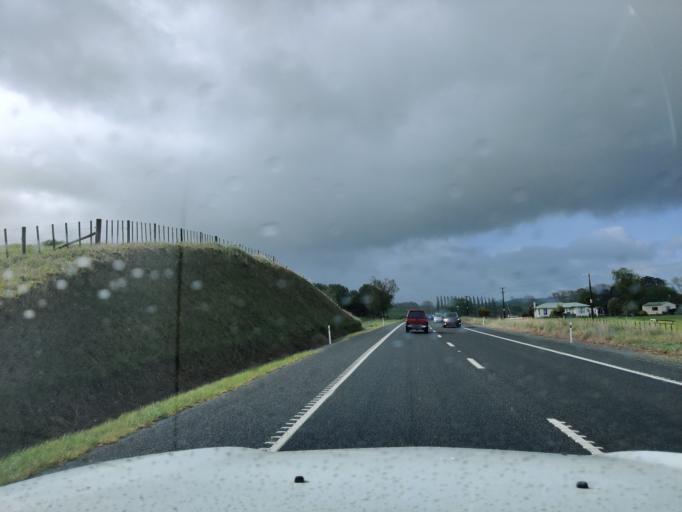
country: NZ
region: Waikato
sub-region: Matamata-Piako District
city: Matamata
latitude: -37.9615
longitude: 175.6874
